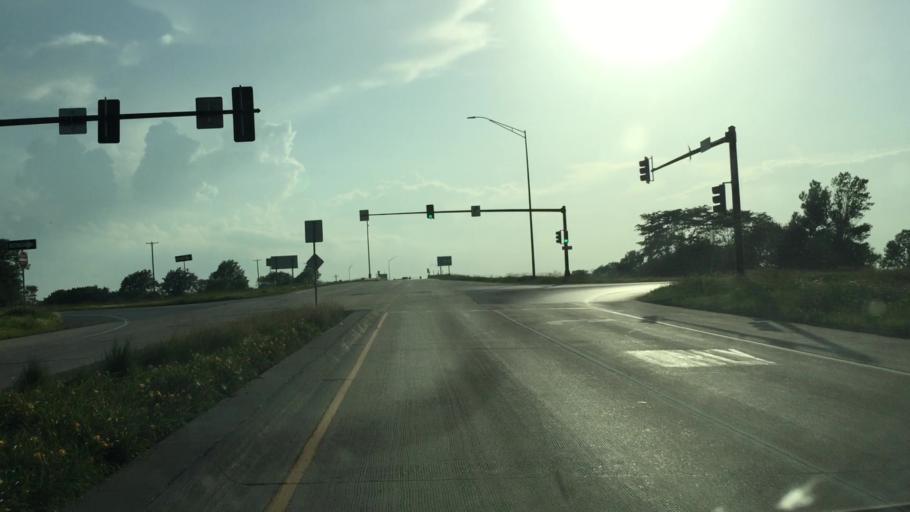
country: US
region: Iowa
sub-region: Johnson County
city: North Liberty
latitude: 41.7525
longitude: -91.6395
